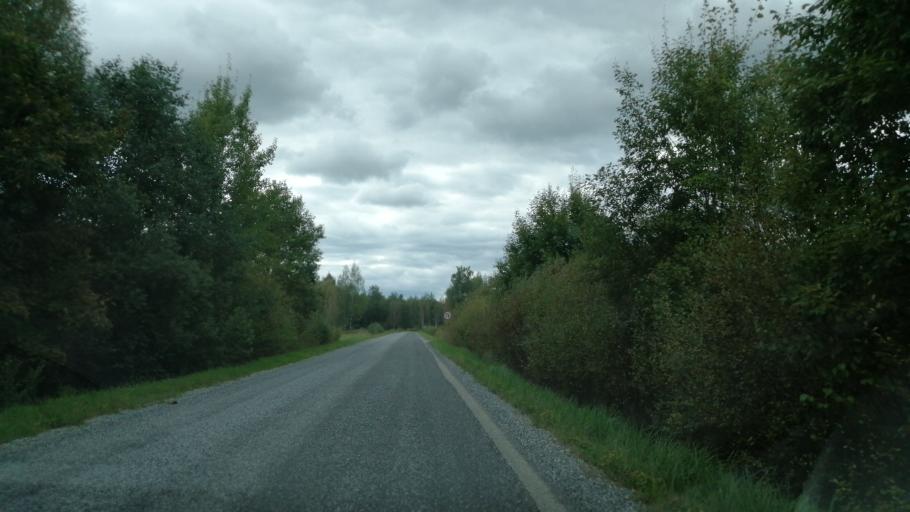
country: EE
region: Jaervamaa
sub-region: Tueri vald
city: Tueri
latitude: 58.8055
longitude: 25.4554
